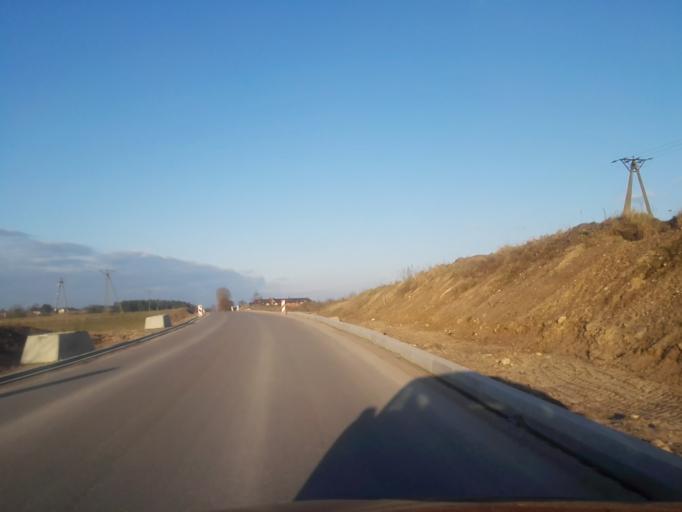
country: PL
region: Podlasie
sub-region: Suwalki
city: Suwalki
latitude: 54.0780
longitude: 23.0629
